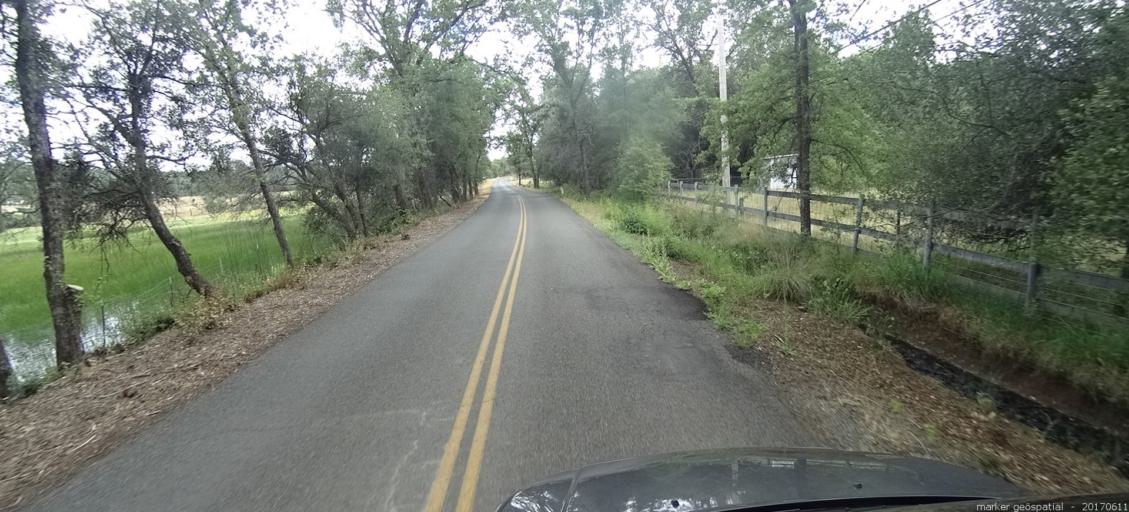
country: US
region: California
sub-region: Butte County
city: Oroville
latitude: 39.6301
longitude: -121.5287
